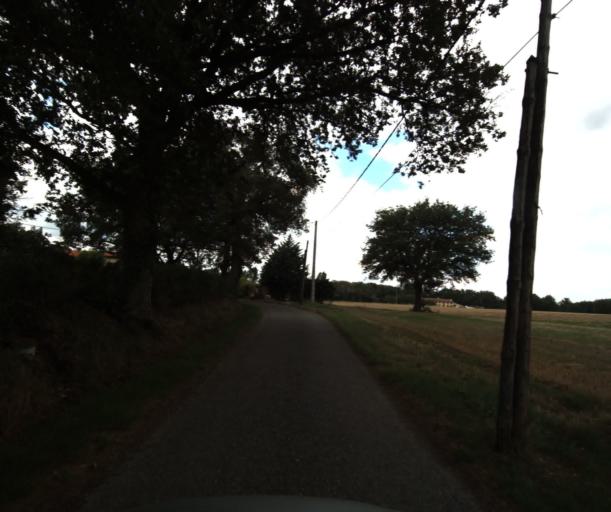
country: FR
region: Midi-Pyrenees
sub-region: Departement de la Haute-Garonne
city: Eaunes
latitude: 43.4198
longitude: 1.3633
